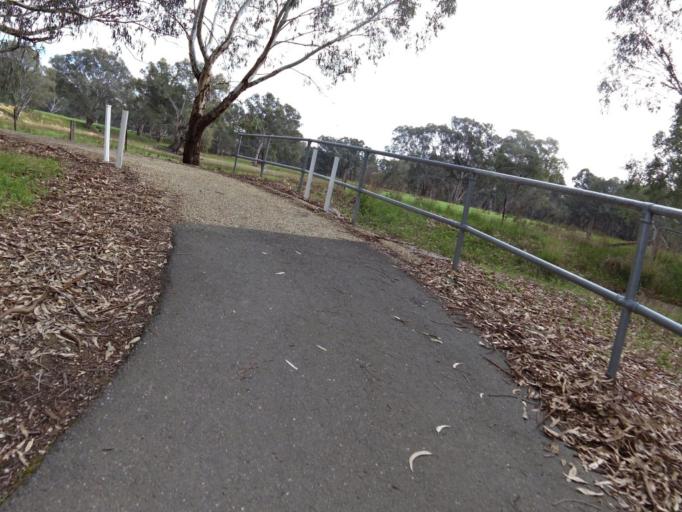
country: AU
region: Victoria
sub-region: Wangaratta
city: Wangaratta
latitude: -36.3905
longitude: 146.3440
